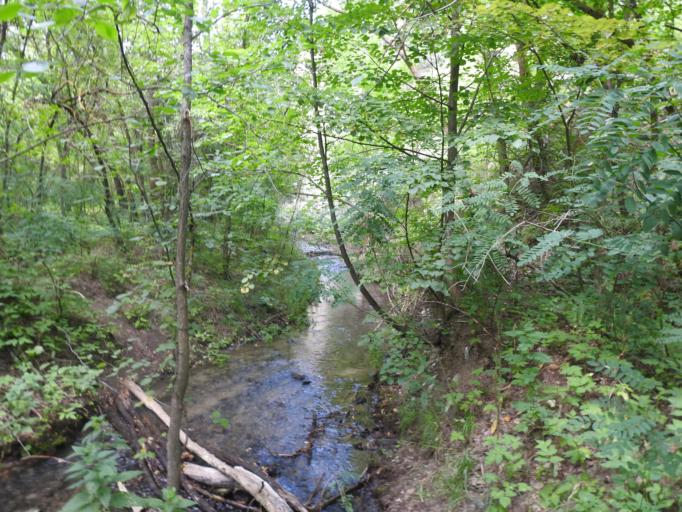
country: RU
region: Saratov
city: Kamenskiy
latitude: 50.4933
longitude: 45.7008
